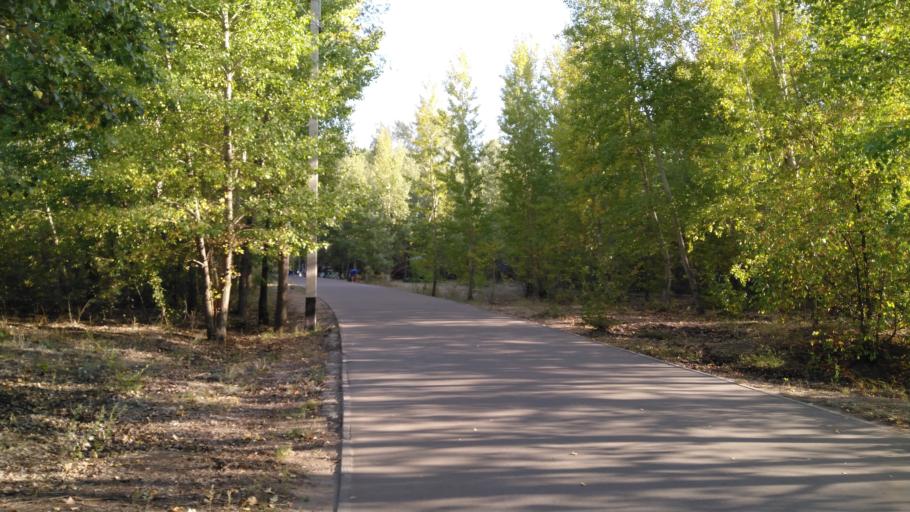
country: KZ
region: Pavlodar
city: Pavlodar
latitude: 52.2596
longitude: 76.9372
